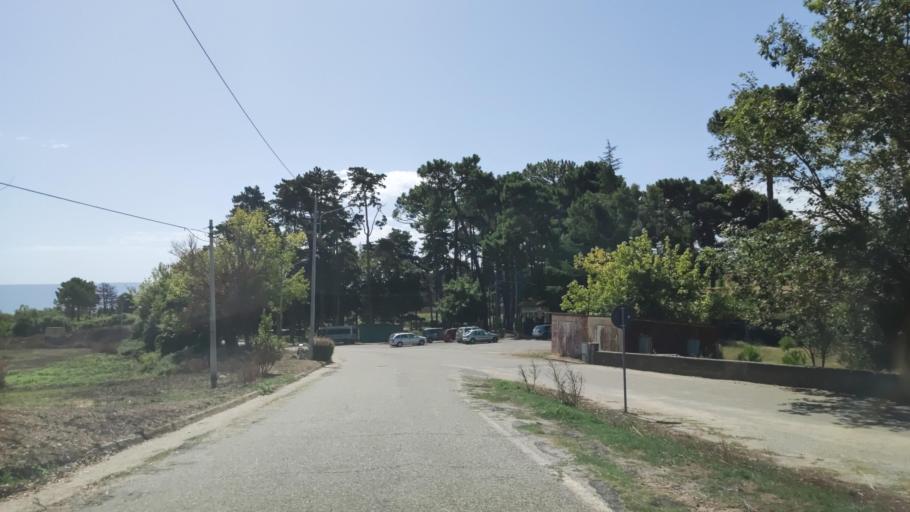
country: IT
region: Calabria
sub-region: Provincia di Reggio Calabria
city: Seminara
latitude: 38.3462
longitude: 15.8411
